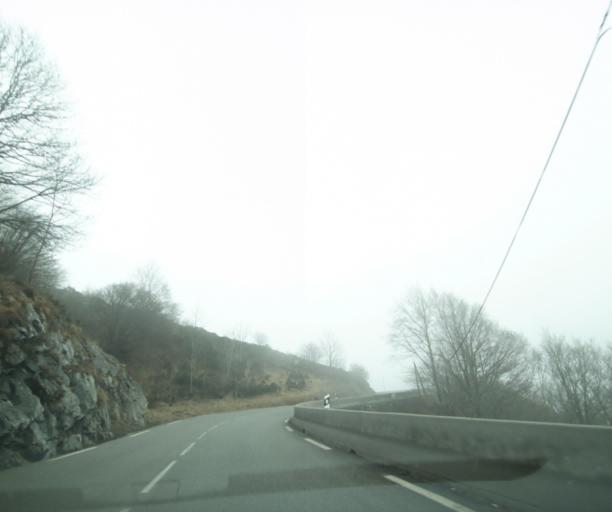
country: FR
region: Languedoc-Roussillon
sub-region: Departement de la Lozere
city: Langogne
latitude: 44.6943
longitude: 4.0303
